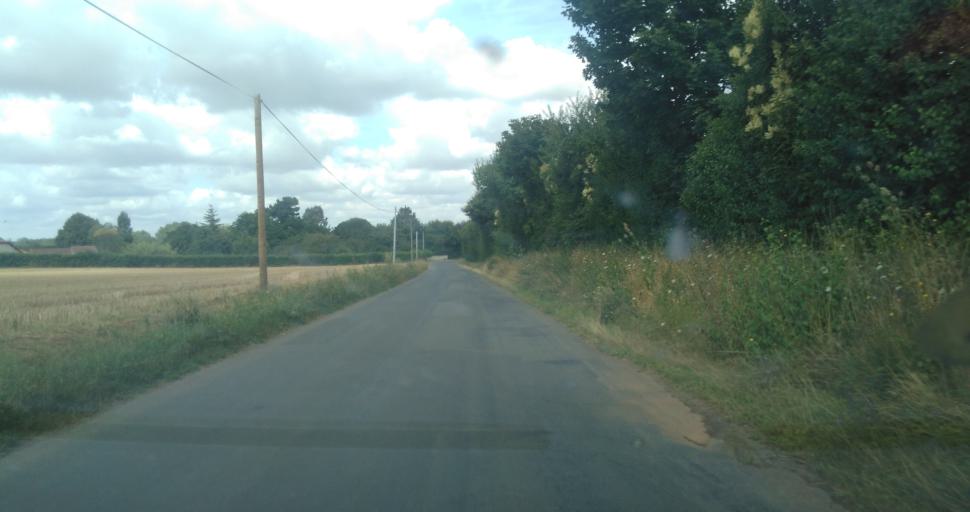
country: FR
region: Pays de la Loire
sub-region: Departement de la Vendee
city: Sainte-Hermine
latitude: 46.5320
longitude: -1.0830
